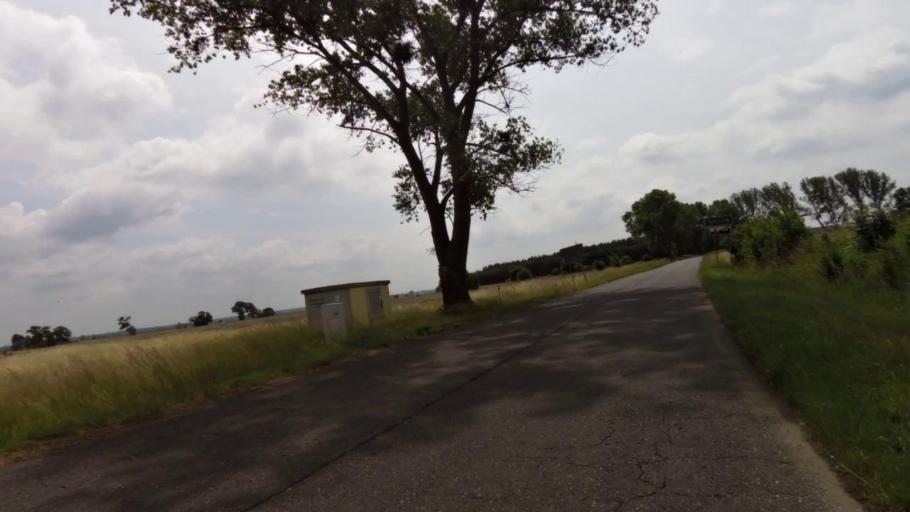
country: PL
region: West Pomeranian Voivodeship
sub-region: Powiat goleniowski
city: Goleniow
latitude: 53.4985
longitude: 14.7105
